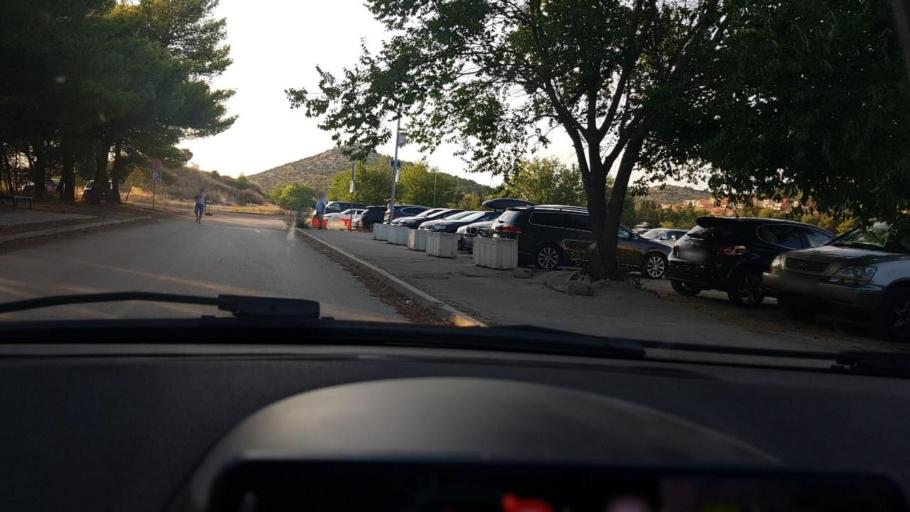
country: HR
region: Sibensko-Kniniska
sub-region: Grad Sibenik
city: Sibenik
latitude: 43.7426
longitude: 15.8849
